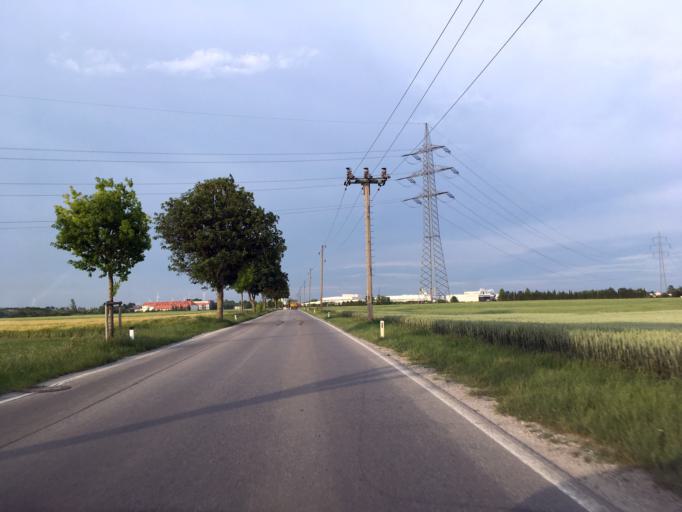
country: AT
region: Lower Austria
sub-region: Politischer Bezirk Wien-Umgebung
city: Gerasdorf bei Wien
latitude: 48.3009
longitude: 16.4757
